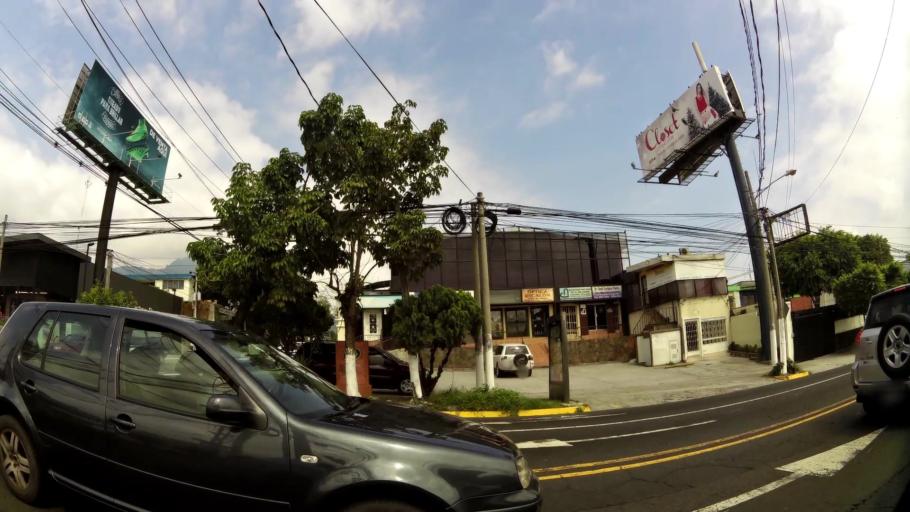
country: SV
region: La Libertad
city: Antiguo Cuscatlan
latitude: 13.7027
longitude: -89.2397
